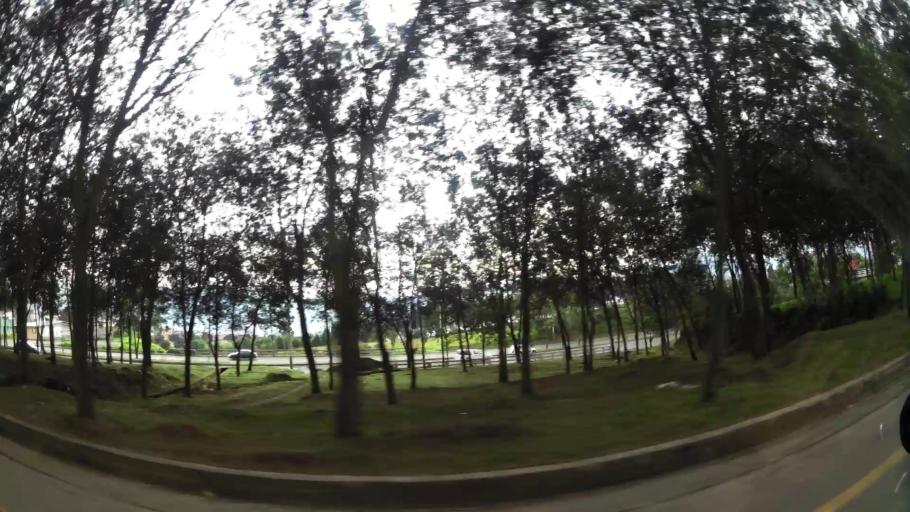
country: EC
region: Pichincha
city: Quito
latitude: -0.2895
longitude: -78.5191
